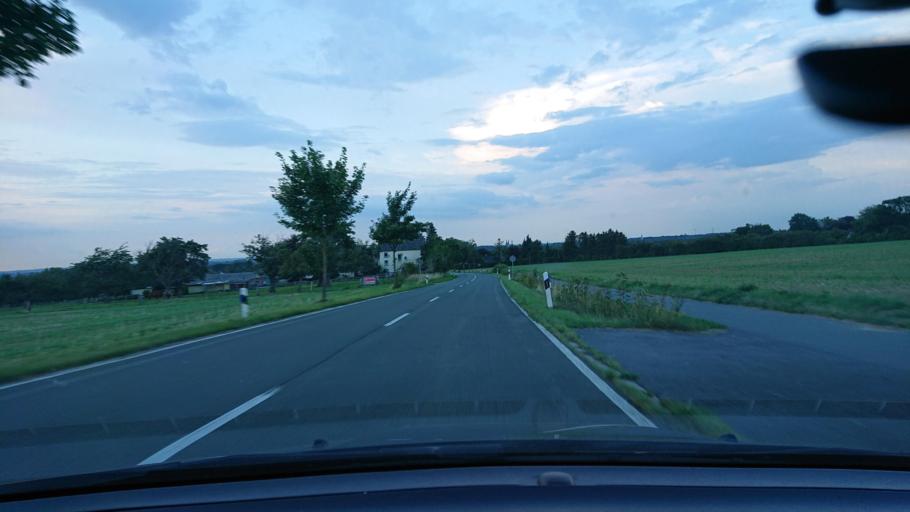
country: DE
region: North Rhine-Westphalia
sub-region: Regierungsbezirk Arnsberg
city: Soest
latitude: 51.5469
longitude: 8.0881
